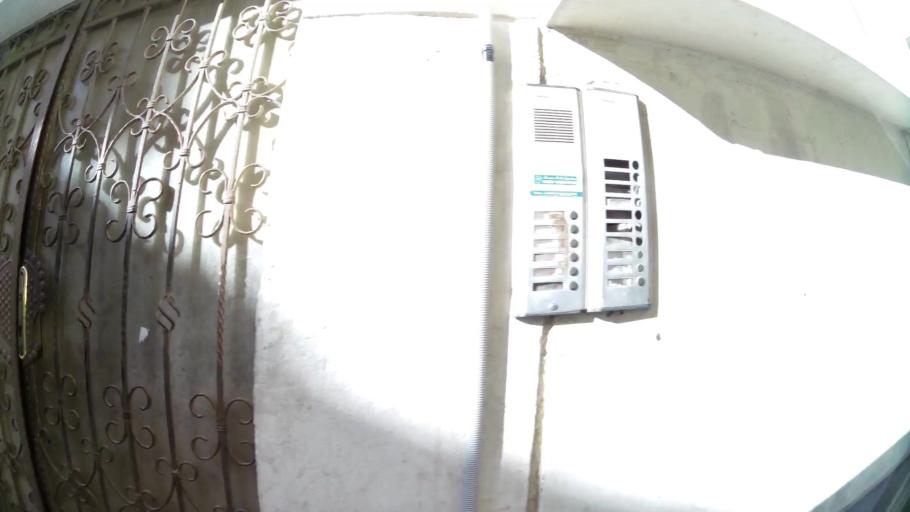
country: BH
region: Manama
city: Manama
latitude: 26.2318
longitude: 50.5863
